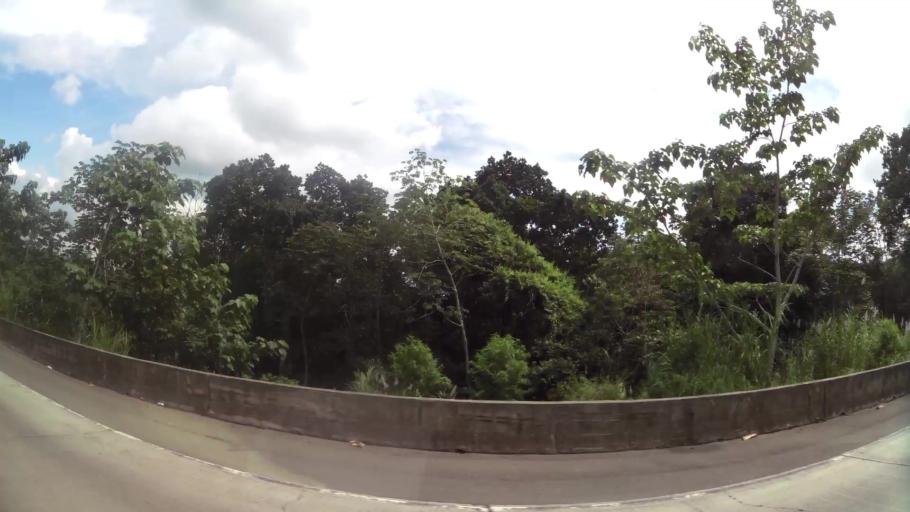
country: PA
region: Panama
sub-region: Distrito de Panama
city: Paraiso
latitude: 9.0091
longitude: -79.6479
